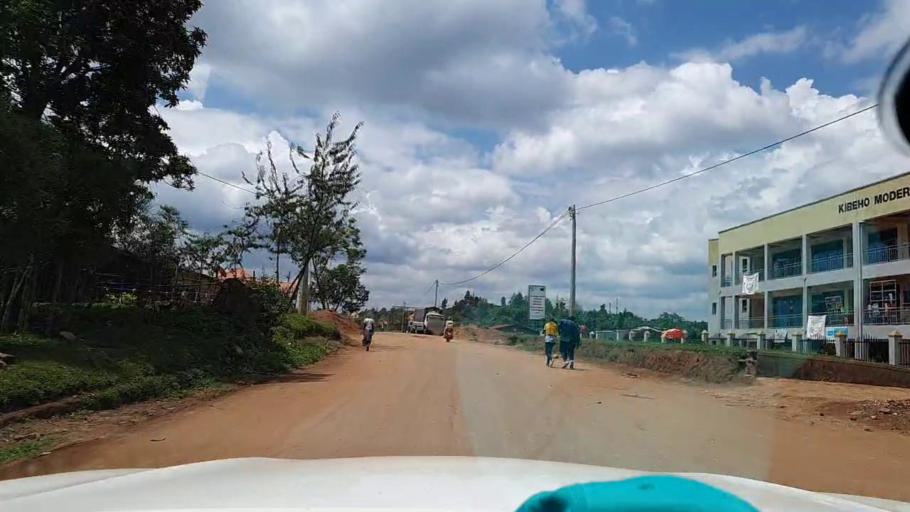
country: RW
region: Southern Province
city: Nzega
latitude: -2.6483
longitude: 29.5610
